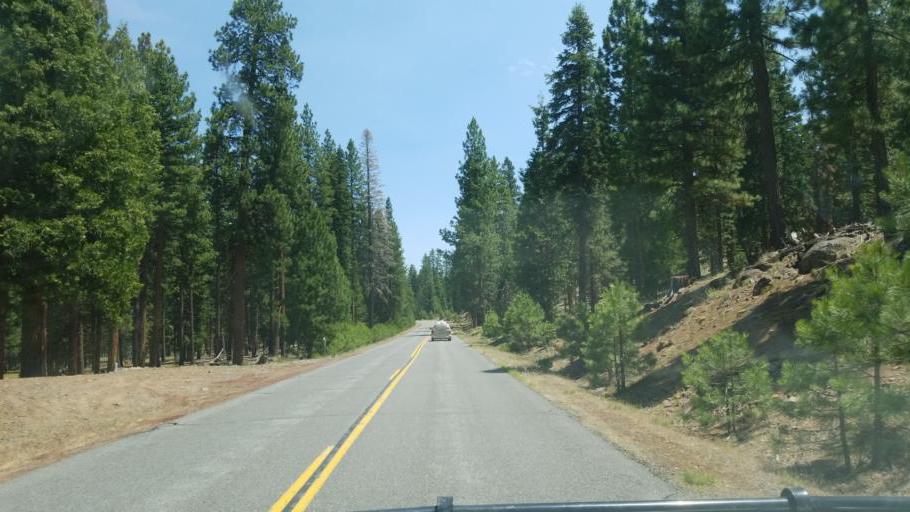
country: US
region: California
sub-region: Lassen County
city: Susanville
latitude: 40.5534
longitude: -120.8227
